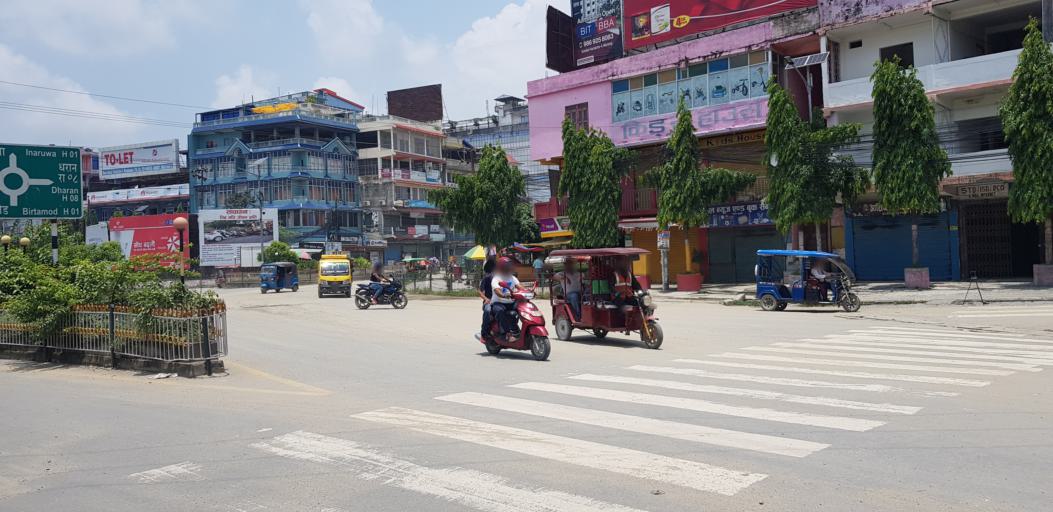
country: NP
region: Eastern Region
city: Ithari
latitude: 26.6631
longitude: 87.2750
